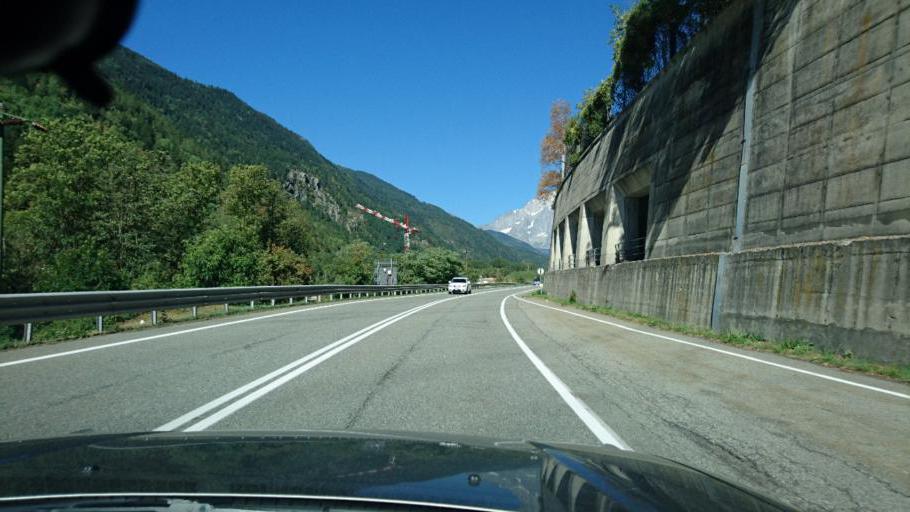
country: IT
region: Aosta Valley
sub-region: Valle d'Aosta
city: Avise
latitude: 45.7177
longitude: 7.1085
